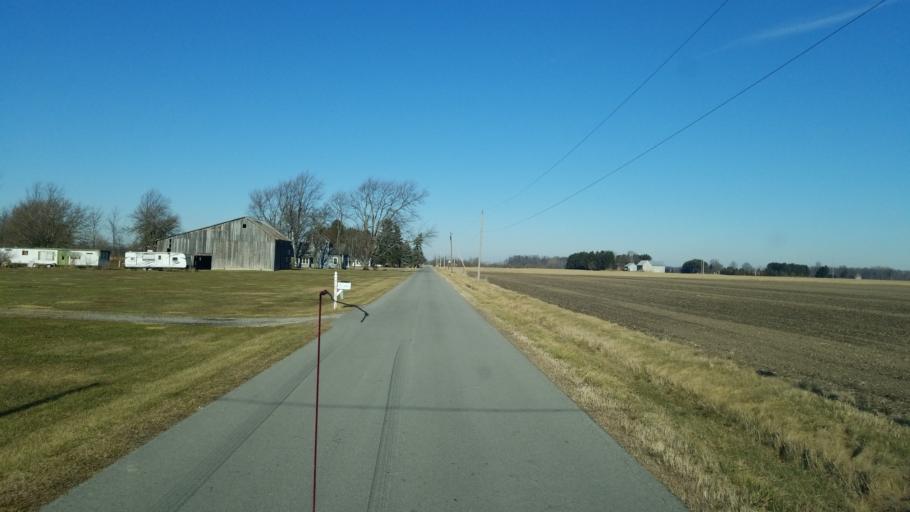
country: US
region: Ohio
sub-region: Henry County
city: Liberty Center
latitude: 41.3764
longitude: -83.9705
